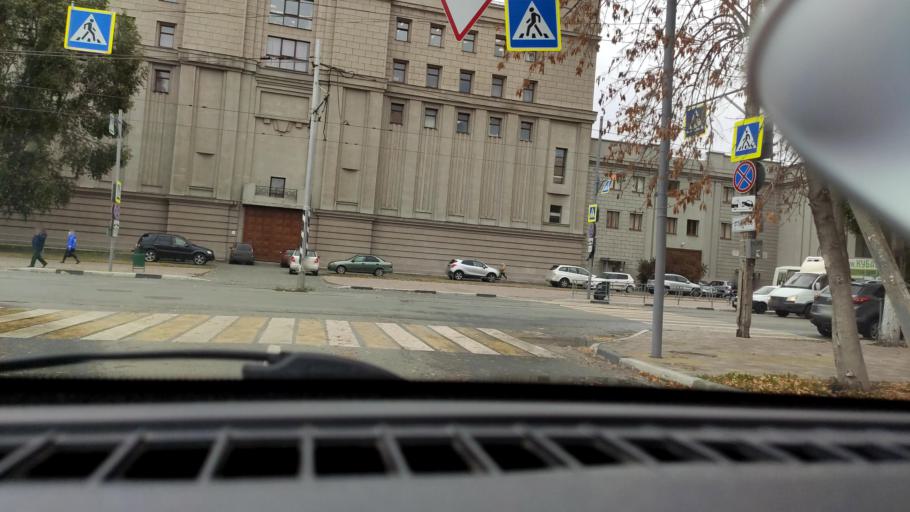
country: RU
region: Samara
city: Samara
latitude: 53.1949
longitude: 50.1047
